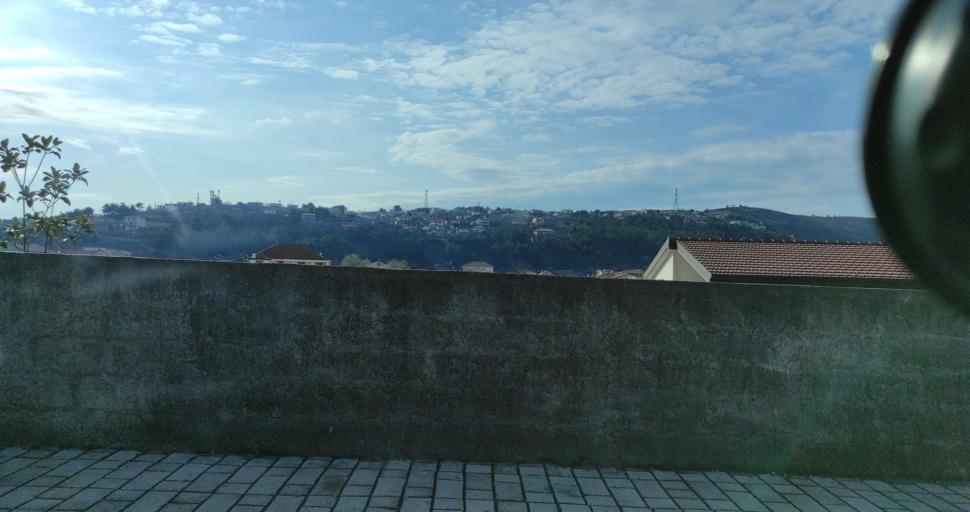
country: AL
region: Lezhe
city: Lezhe
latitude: 41.7883
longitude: 19.6460
